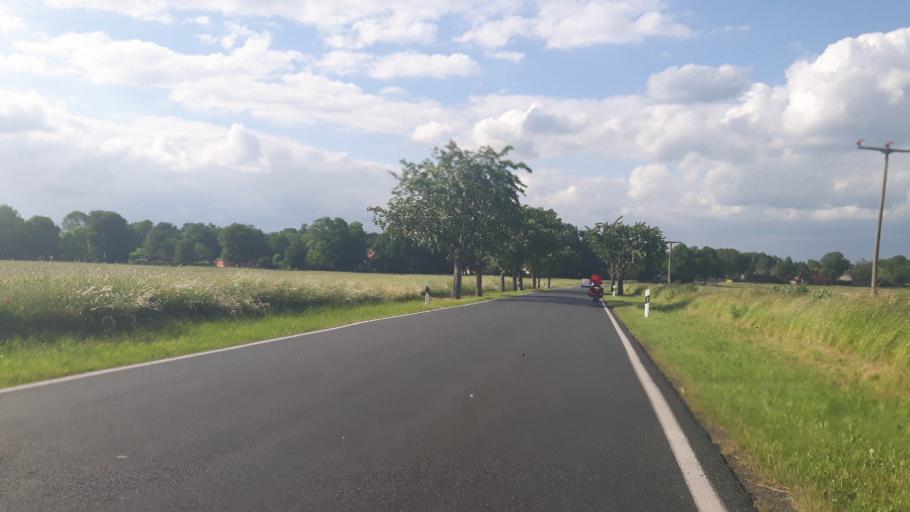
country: DE
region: Brandenburg
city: Melchow
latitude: 52.7327
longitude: 13.7100
